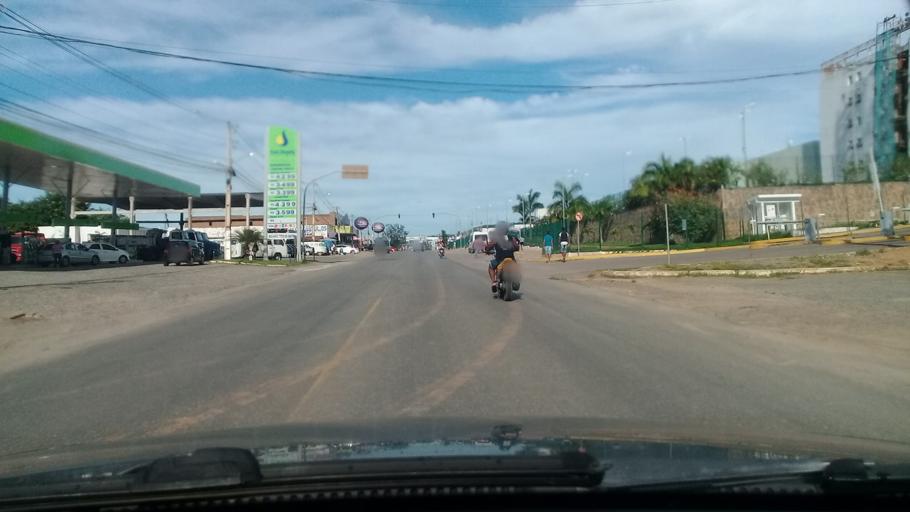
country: BR
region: Pernambuco
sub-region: Vitoria De Santo Antao
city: Vitoria de Santo Antao
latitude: -8.1153
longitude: -35.2726
